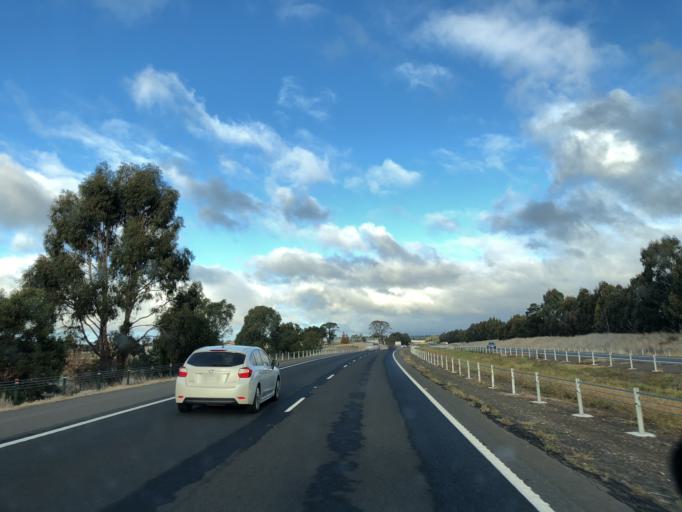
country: AU
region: Victoria
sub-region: Mount Alexander
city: Castlemaine
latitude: -37.2289
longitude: 144.4437
